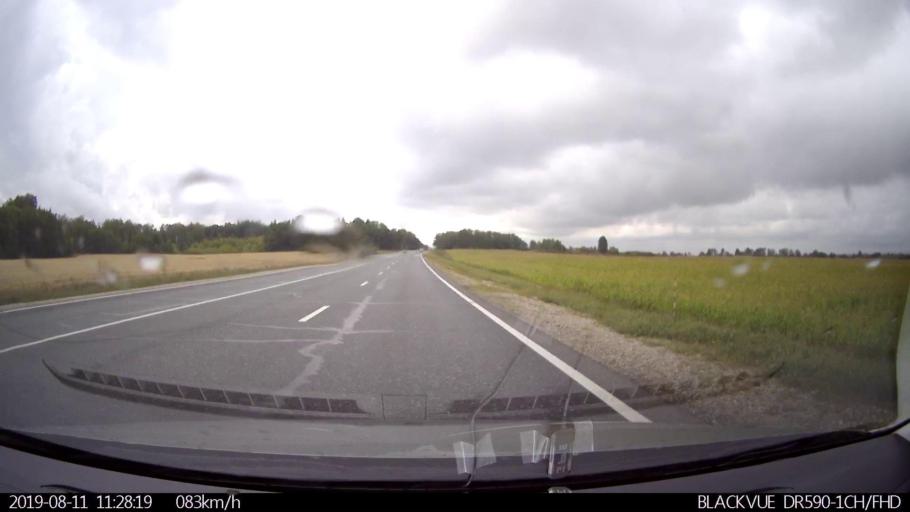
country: RU
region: Ulyanovsk
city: Krasnyy Gulyay
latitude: 54.0826
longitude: 48.2287
